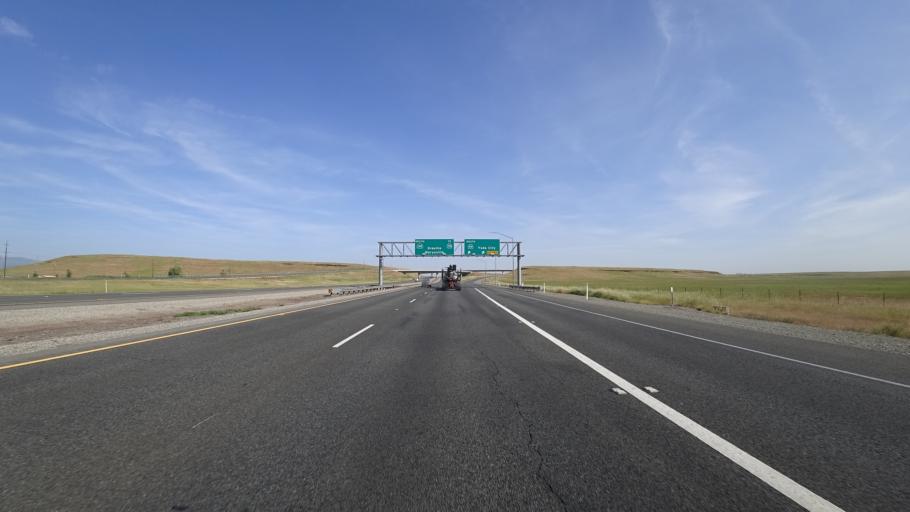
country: US
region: California
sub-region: Butte County
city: Durham
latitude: 39.6258
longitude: -121.6975
